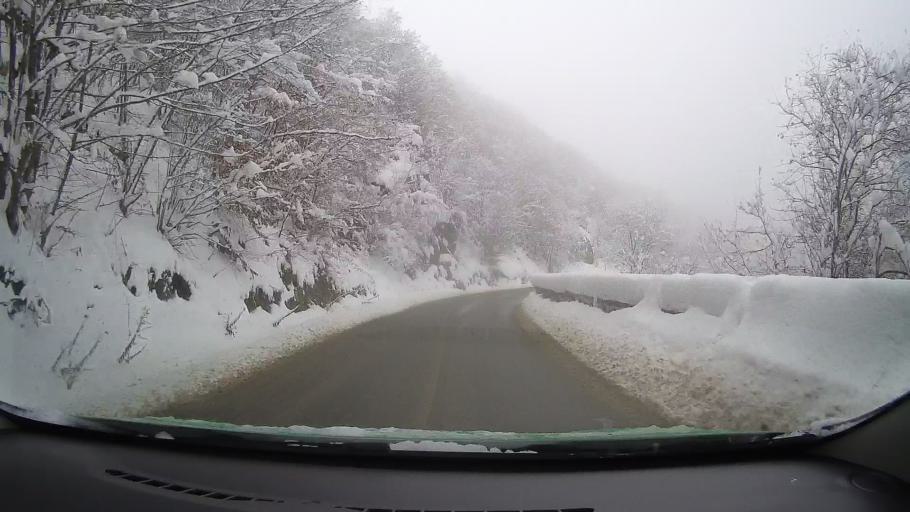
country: RO
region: Sibiu
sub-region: Comuna Tilisca
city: Tilisca
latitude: 45.7976
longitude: 23.7931
